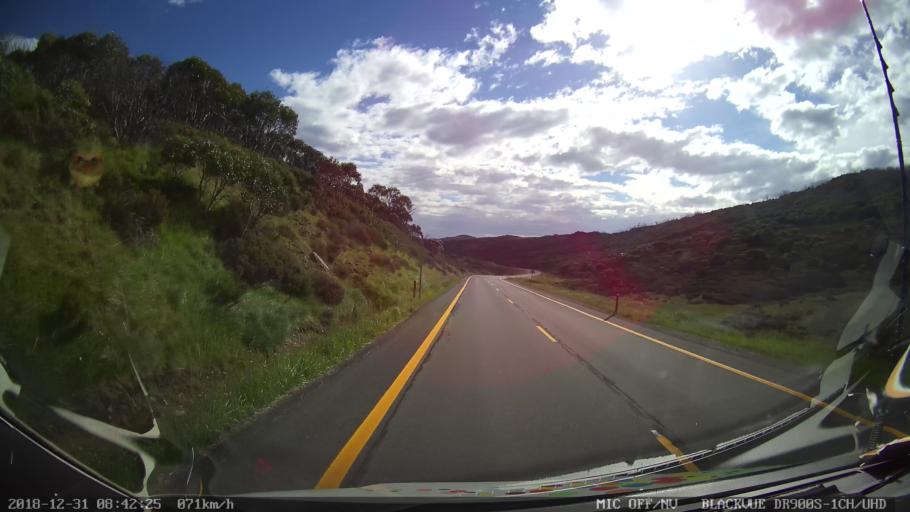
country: AU
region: New South Wales
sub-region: Snowy River
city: Jindabyne
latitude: -36.3935
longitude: 148.4321
